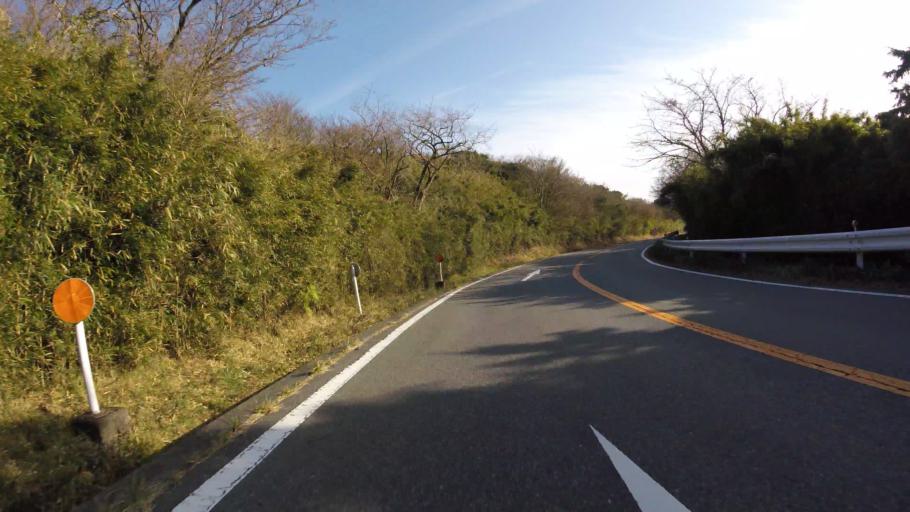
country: JP
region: Kanagawa
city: Hakone
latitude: 35.1478
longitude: 139.0292
